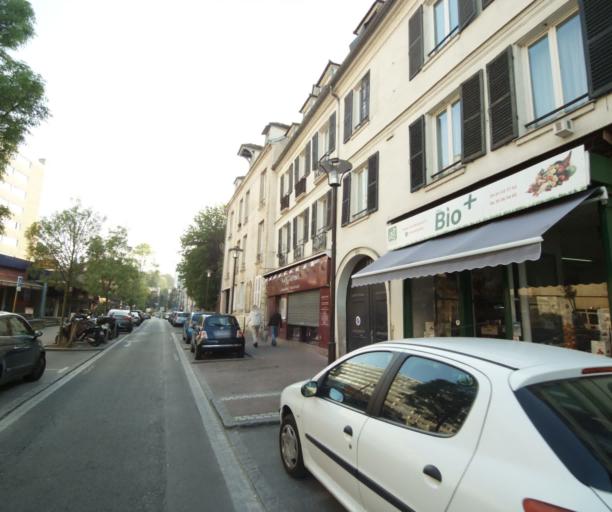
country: FR
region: Ile-de-France
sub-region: Departement des Hauts-de-Seine
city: Sevres
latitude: 48.8232
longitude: 2.2079
